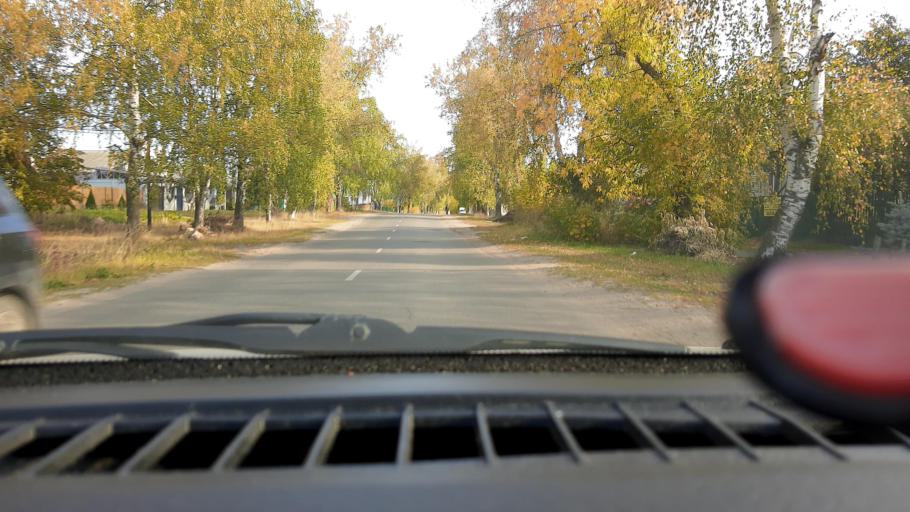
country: RU
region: Nizjnij Novgorod
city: Lukino
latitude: 56.4059
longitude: 43.7095
